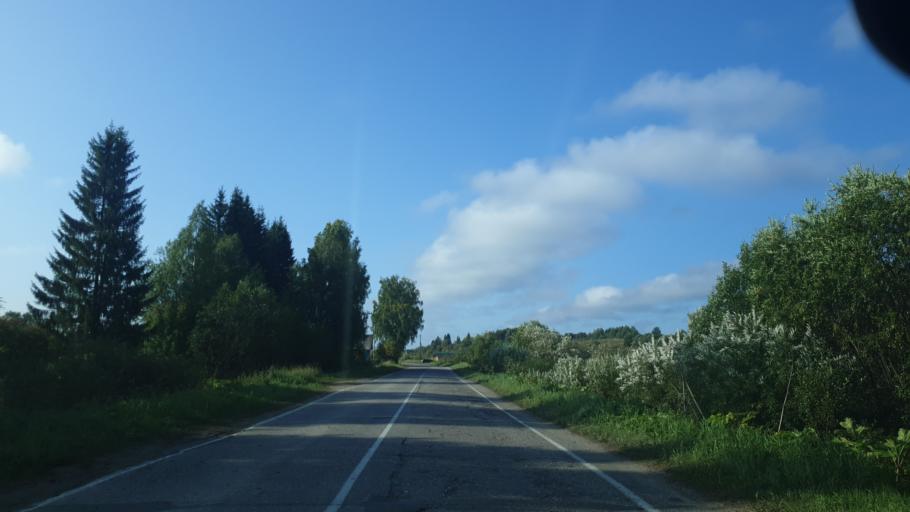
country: RU
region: Komi Republic
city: Vizinga
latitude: 60.9306
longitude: 50.2239
